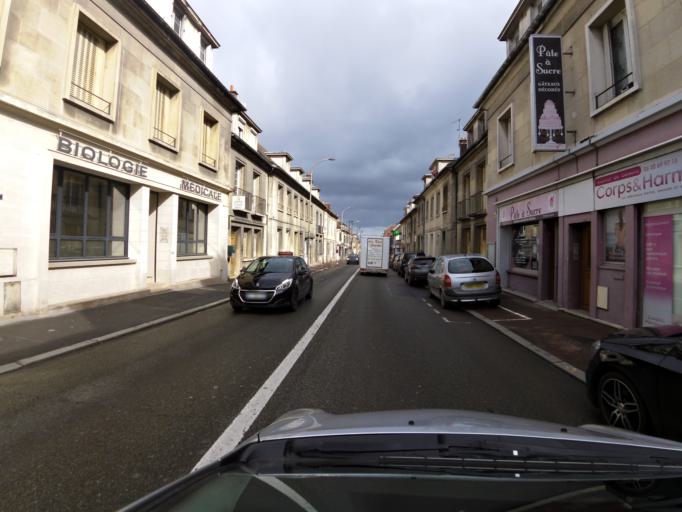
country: FR
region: Picardie
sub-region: Departement de l'Oise
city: Pont-Sainte-Maxence
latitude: 49.3036
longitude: 2.6043
